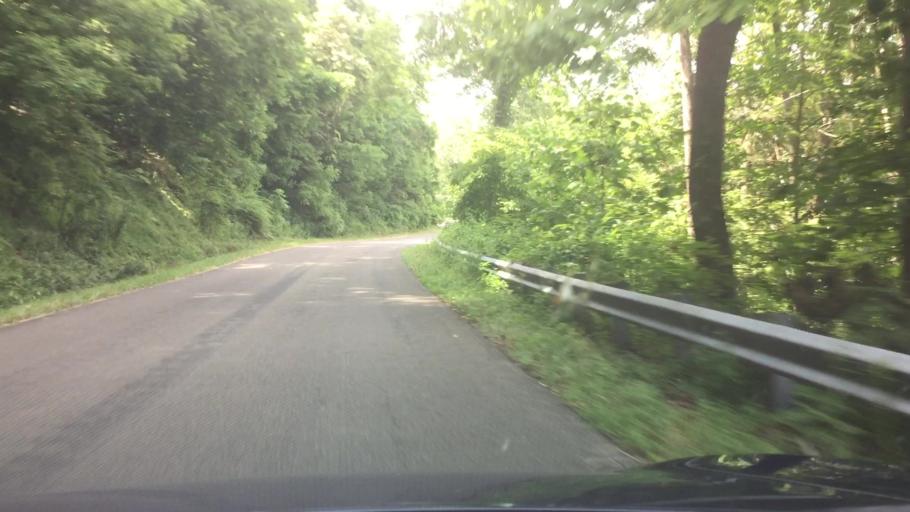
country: US
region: Virginia
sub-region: Wythe County
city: Wytheville
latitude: 36.9318
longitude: -81.0697
